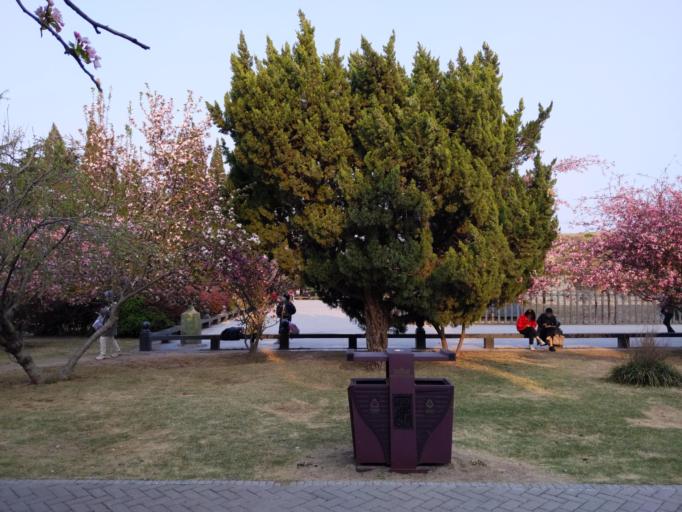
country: CN
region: Henan Sheng
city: Puyang
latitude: 35.7524
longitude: 115.0283
